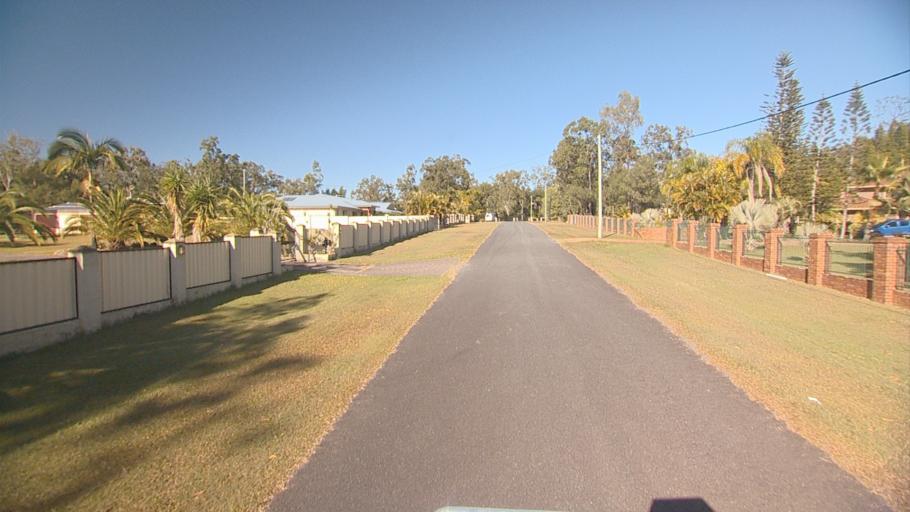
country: AU
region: Queensland
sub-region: Logan
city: Chambers Flat
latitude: -27.7500
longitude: 153.0511
